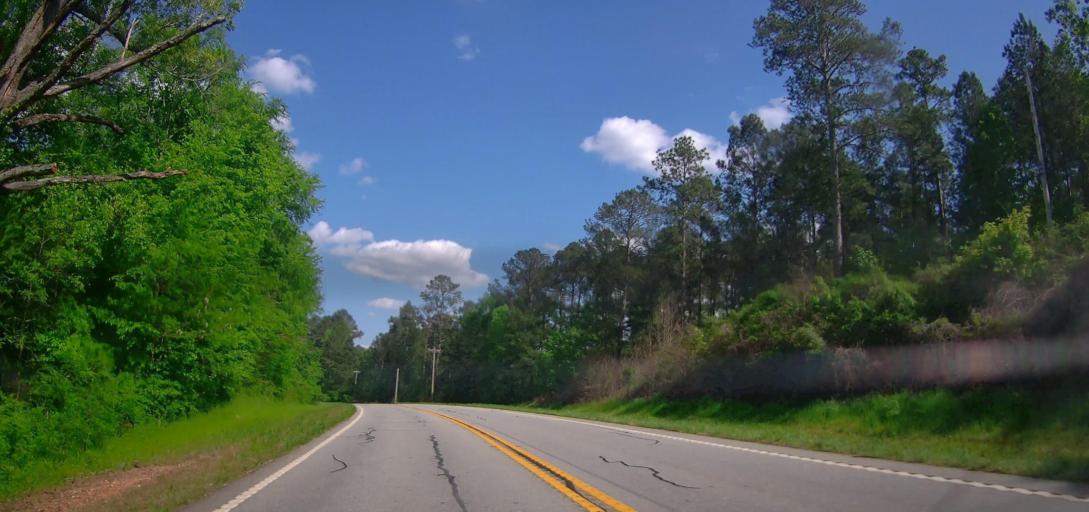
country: US
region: Georgia
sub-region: Greene County
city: Greensboro
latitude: 33.5760
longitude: -83.2621
